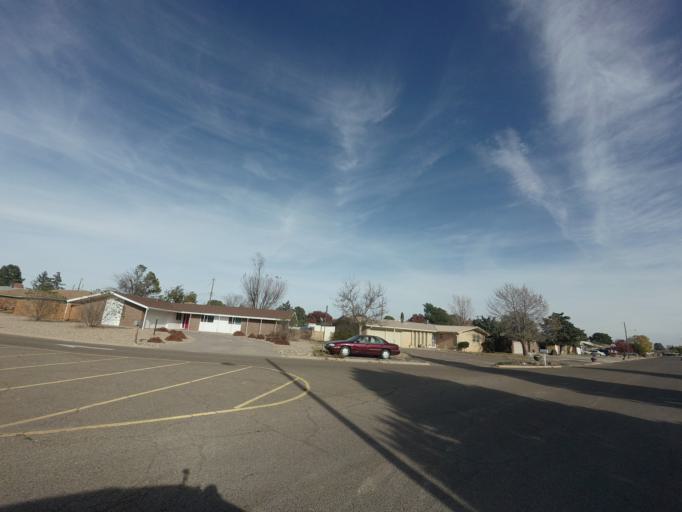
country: US
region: New Mexico
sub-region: Curry County
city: Clovis
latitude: 34.4239
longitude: -103.2225
